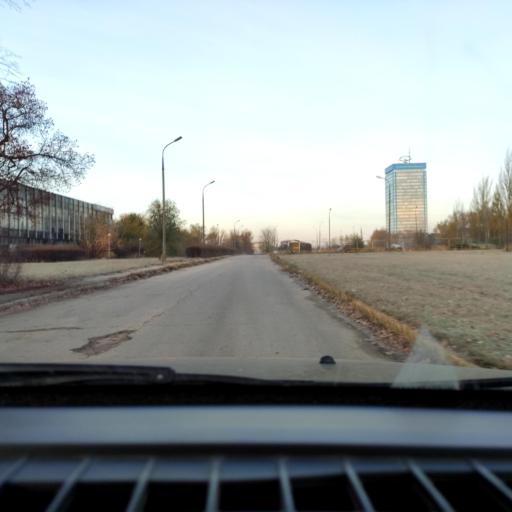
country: RU
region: Samara
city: Tol'yatti
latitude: 53.5535
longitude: 49.2736
